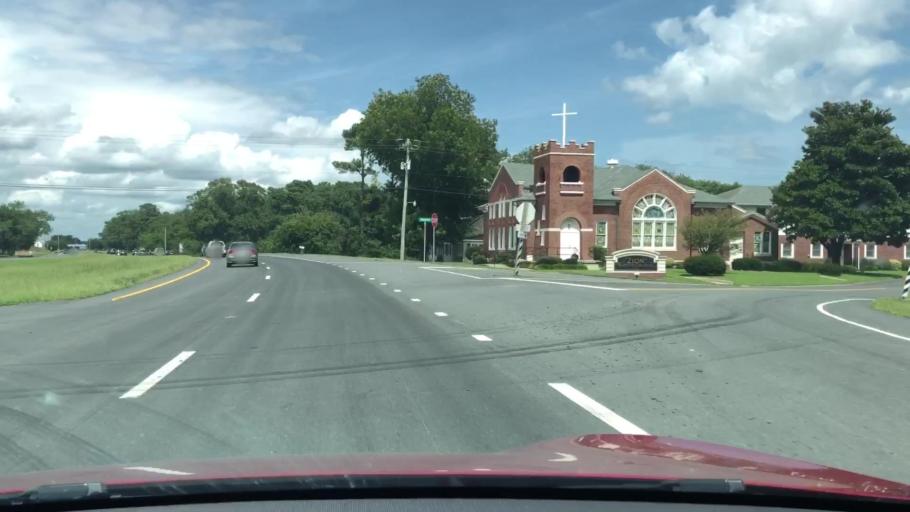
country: US
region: Virginia
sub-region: Accomack County
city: Accomac
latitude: 37.7622
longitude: -75.6155
